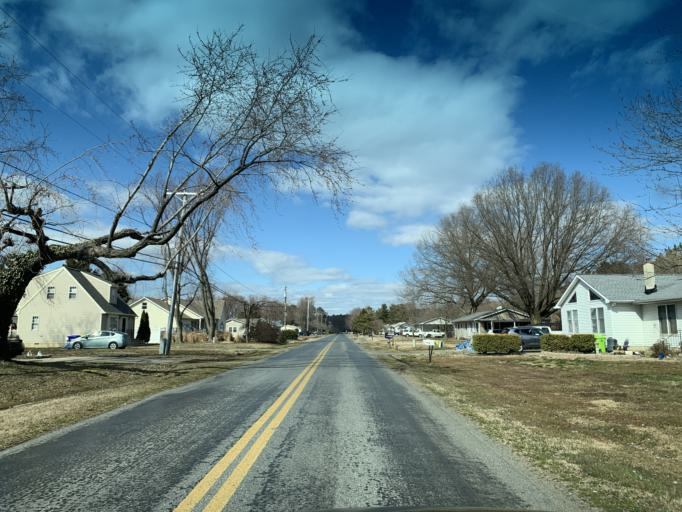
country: US
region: Maryland
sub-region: Queen Anne's County
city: Chester
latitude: 38.9363
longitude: -76.2659
